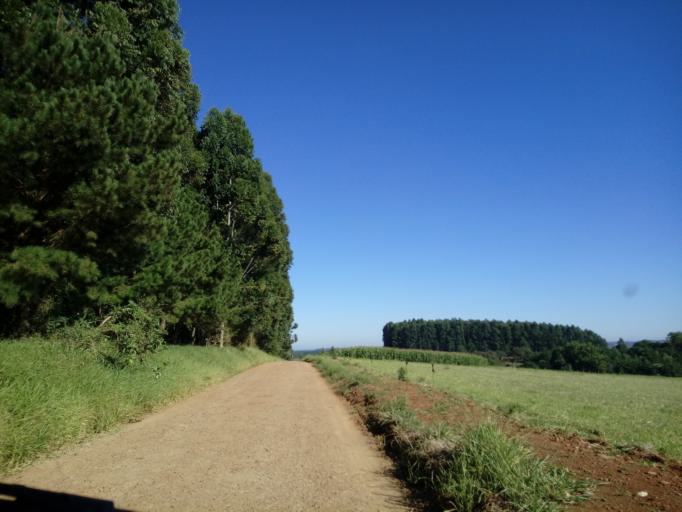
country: BR
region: Santa Catarina
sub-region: Chapeco
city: Chapeco
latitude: -27.1862
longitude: -52.7288
